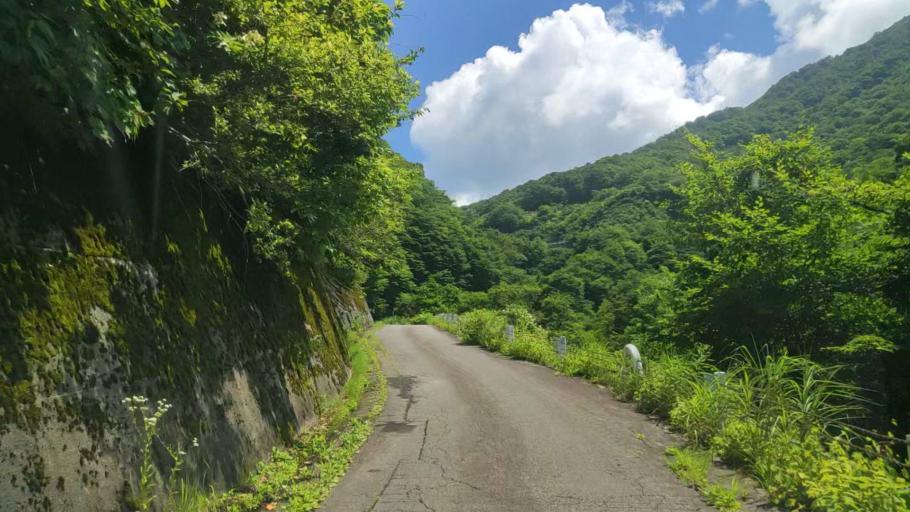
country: JP
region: Fukui
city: Ono
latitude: 35.7835
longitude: 136.5141
